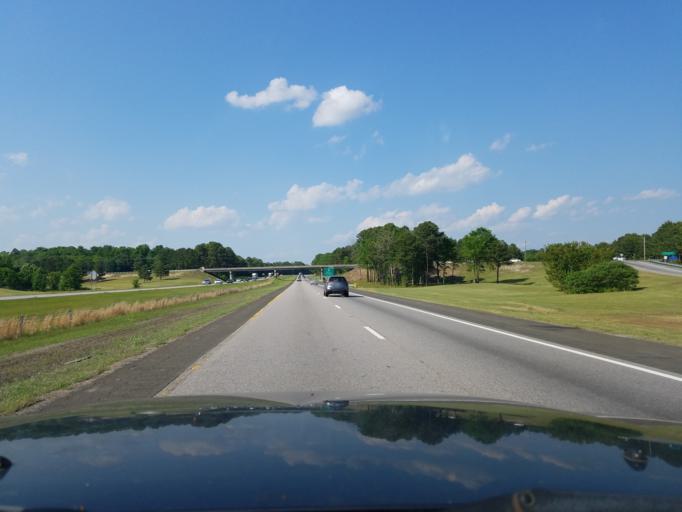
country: US
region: North Carolina
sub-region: Granville County
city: Butner
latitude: 36.1183
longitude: -78.7470
